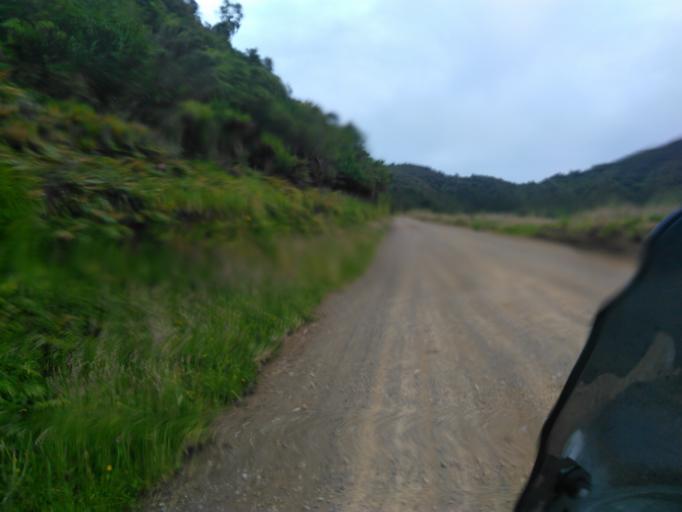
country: NZ
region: Bay of Plenty
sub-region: Opotiki District
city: Opotiki
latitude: -38.0975
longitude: 177.4856
